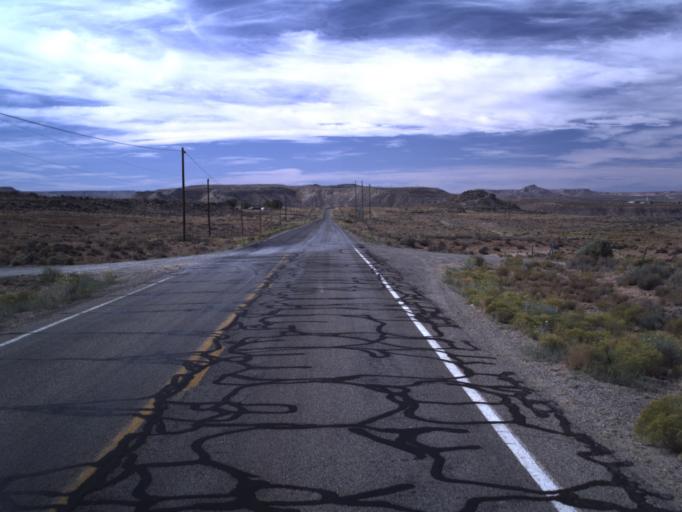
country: US
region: Utah
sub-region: San Juan County
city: Blanding
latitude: 37.2851
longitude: -109.2915
